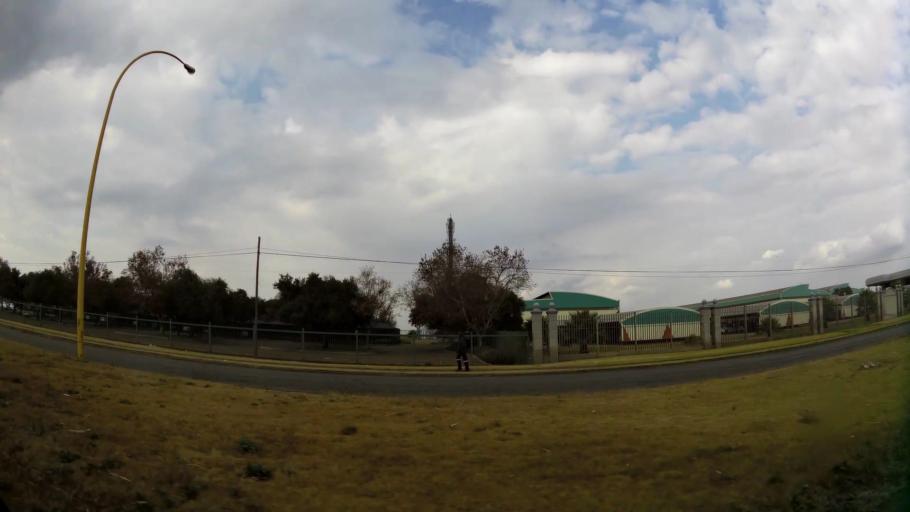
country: ZA
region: Gauteng
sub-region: Sedibeng District Municipality
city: Vanderbijlpark
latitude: -26.6771
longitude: 27.8182
